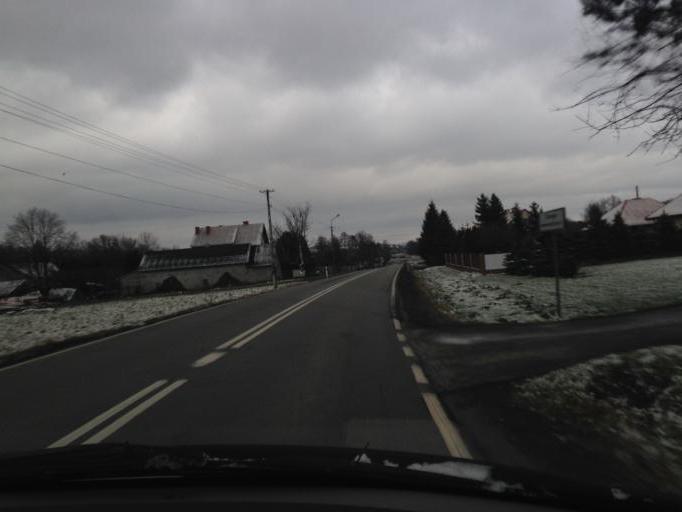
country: PL
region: Lesser Poland Voivodeship
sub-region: Powiat tarnowski
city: Janowice
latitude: 49.8553
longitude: 20.8637
